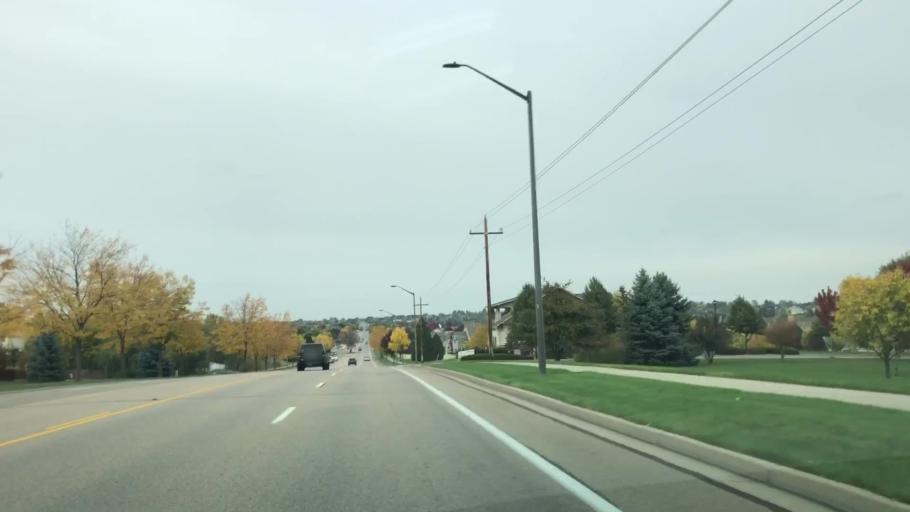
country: US
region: Colorado
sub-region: Larimer County
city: Loveland
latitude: 40.4900
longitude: -105.0582
